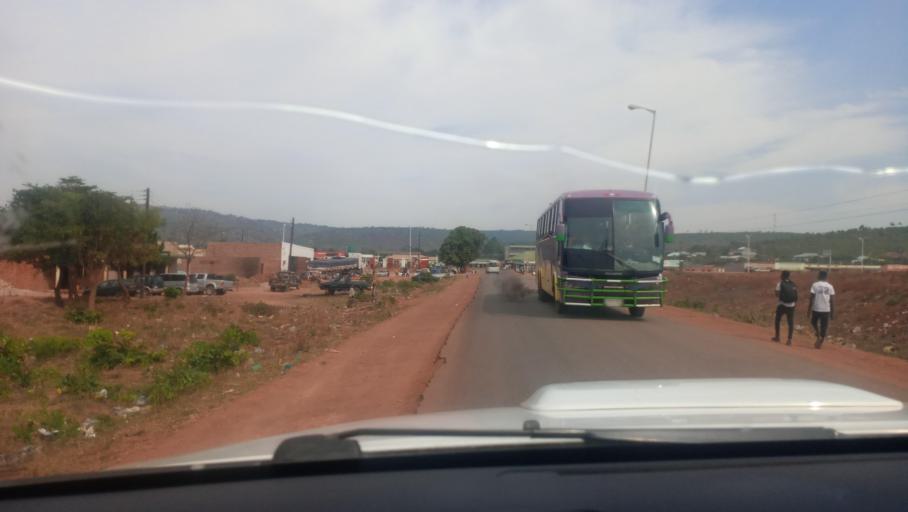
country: ZM
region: Northern
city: Mpika
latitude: -11.8431
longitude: 31.4420
